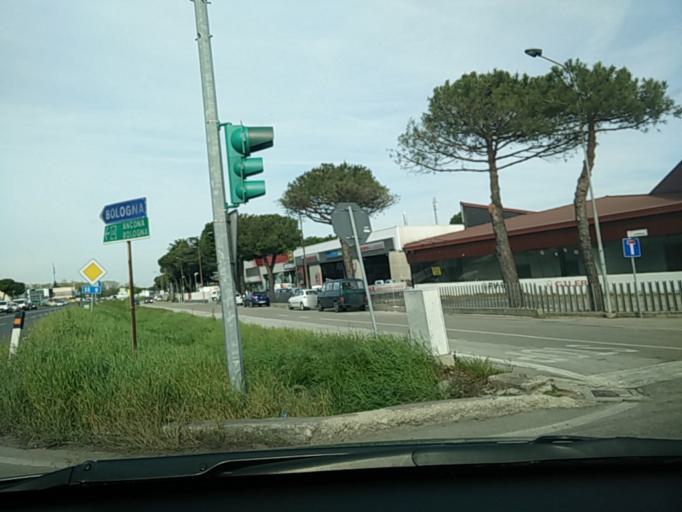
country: IT
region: Emilia-Romagna
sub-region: Provincia di Rimini
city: Rimini
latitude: 44.0645
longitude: 12.5372
